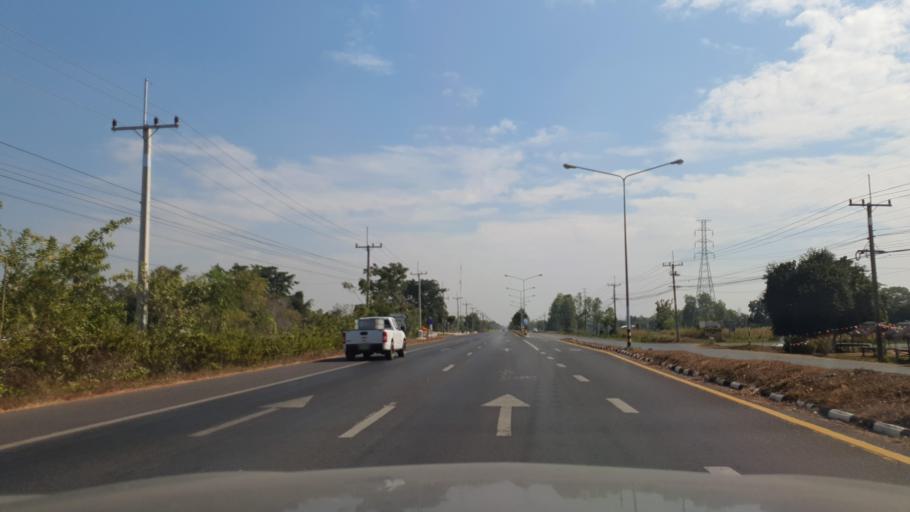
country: TH
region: Maha Sarakham
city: Kantharawichai
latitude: 16.3918
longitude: 103.2818
